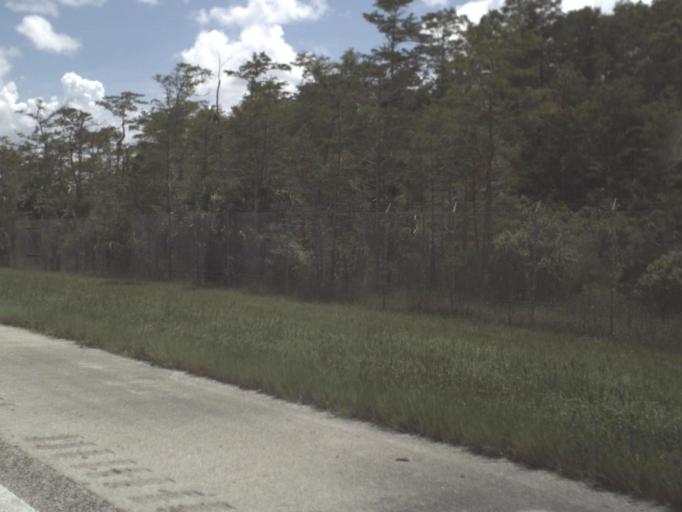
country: US
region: Florida
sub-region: Collier County
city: Immokalee
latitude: 26.1702
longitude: -80.9875
